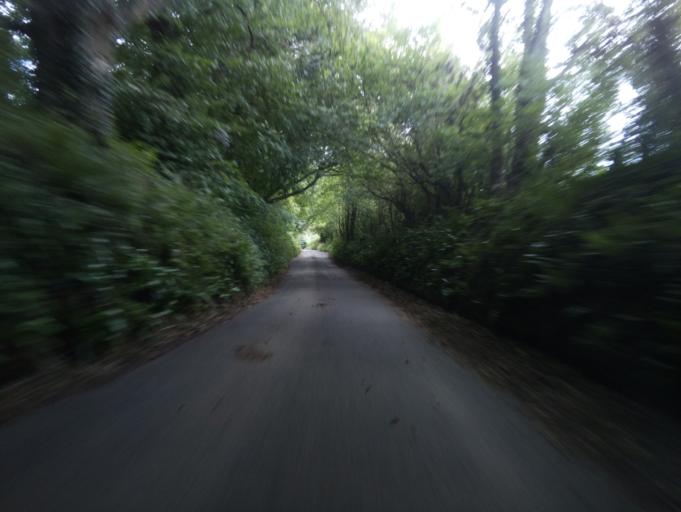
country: GB
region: England
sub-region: Devon
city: Totnes
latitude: 50.3964
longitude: -3.7121
